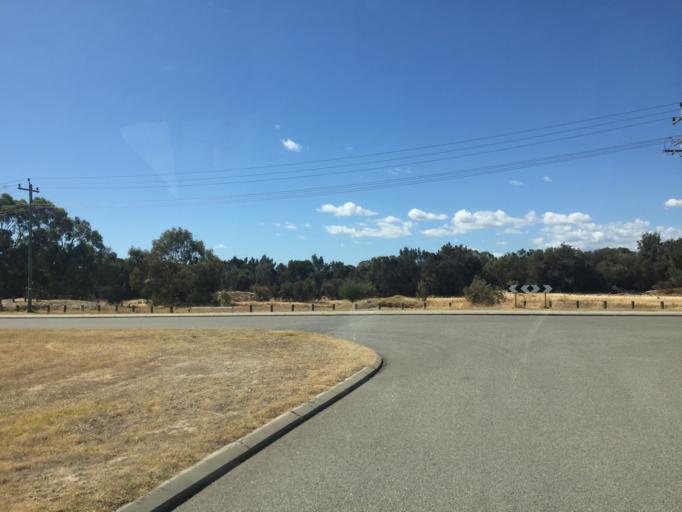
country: AU
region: Western Australia
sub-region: Belmont
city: Redcliffe
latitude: -31.9278
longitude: 115.9434
